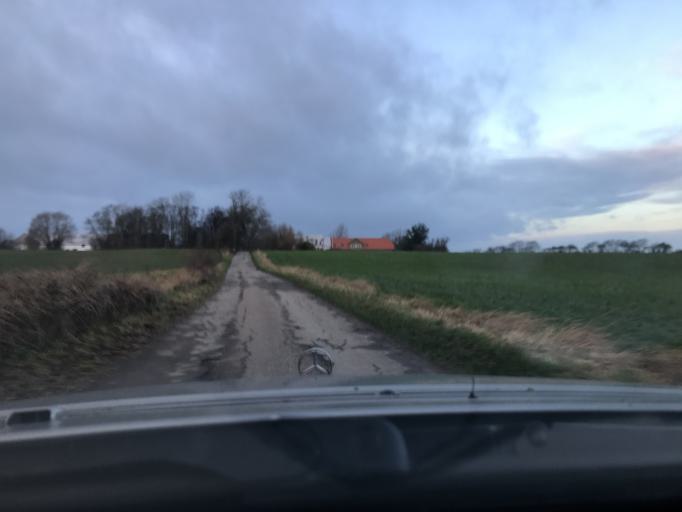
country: DK
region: South Denmark
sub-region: Sonderborg Kommune
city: Nordborg
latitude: 55.0664
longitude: 9.6931
